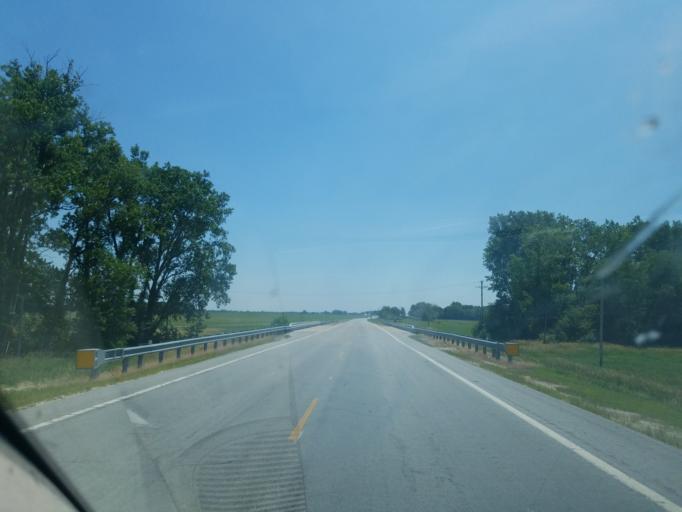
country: US
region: Ohio
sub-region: Mercer County
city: Rockford
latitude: 40.7268
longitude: -84.7388
